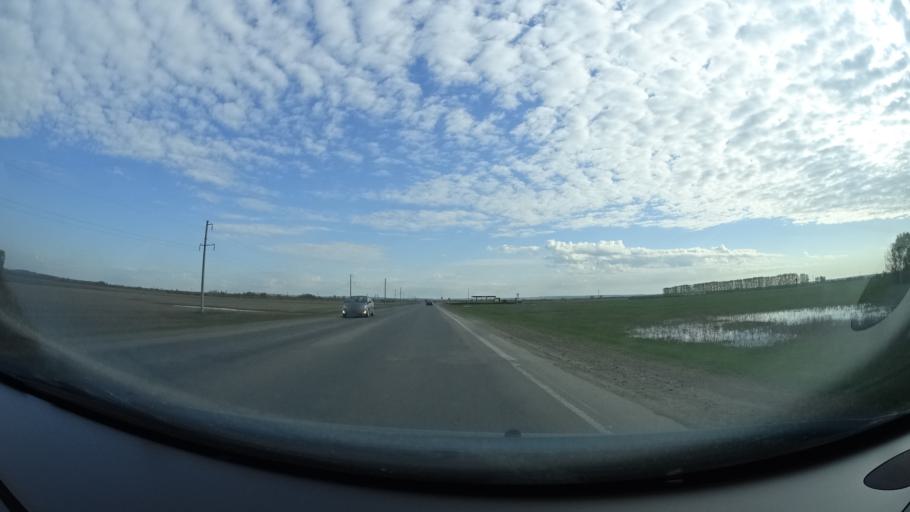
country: RU
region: Bashkortostan
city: Mikhaylovka
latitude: 54.9649
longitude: 55.7621
